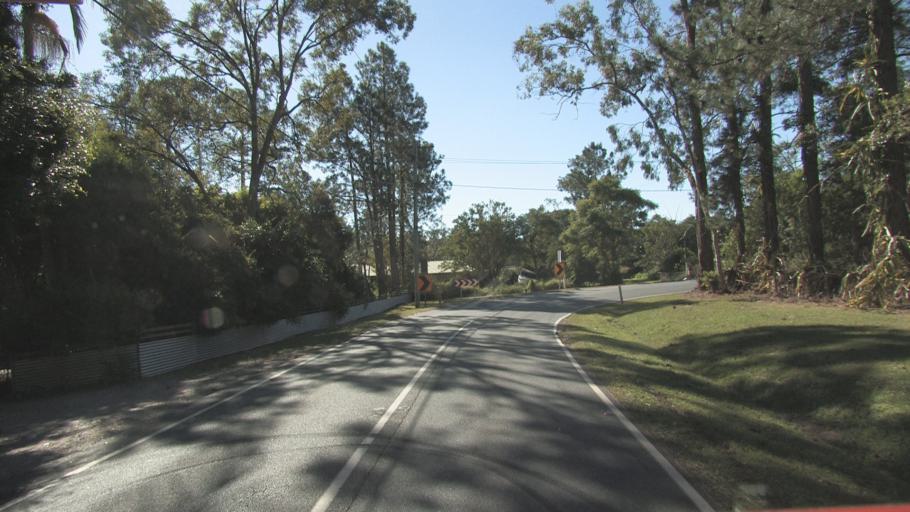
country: AU
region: Queensland
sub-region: Logan
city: Logan Reserve
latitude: -27.7191
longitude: 153.0647
